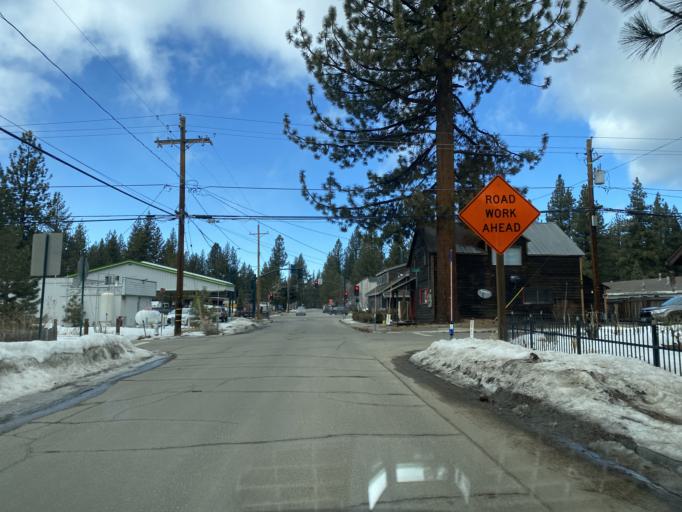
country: US
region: California
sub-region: El Dorado County
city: South Lake Tahoe
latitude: 38.9231
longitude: -119.9881
